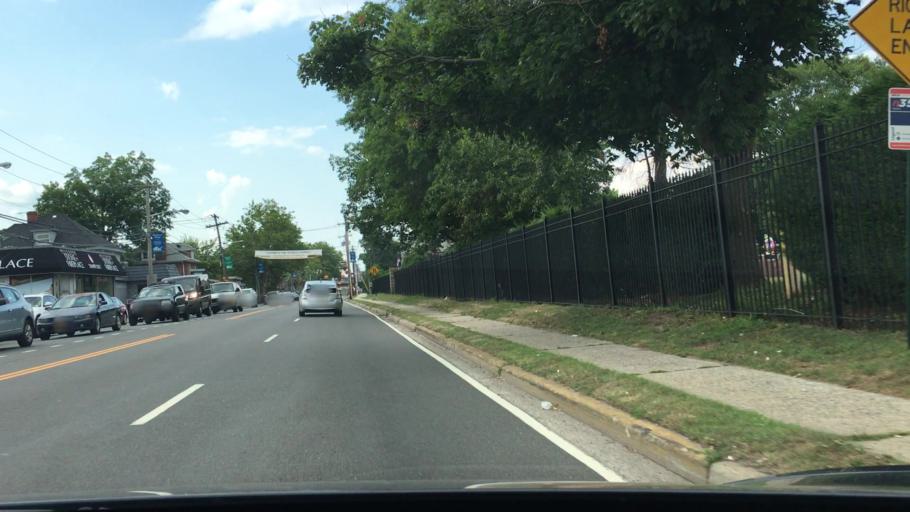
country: US
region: New York
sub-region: Nassau County
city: Westbury
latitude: 40.7484
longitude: -73.5876
